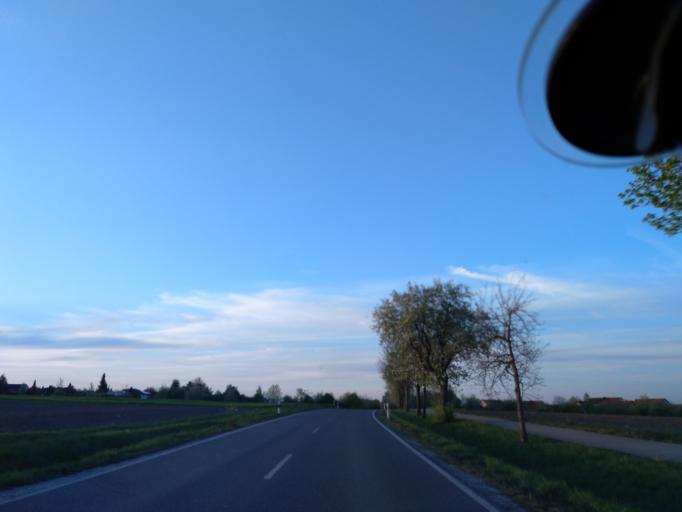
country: DE
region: Baden-Wuerttemberg
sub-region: Regierungsbezirk Stuttgart
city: Satteldorf
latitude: 49.1635
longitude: 10.0795
